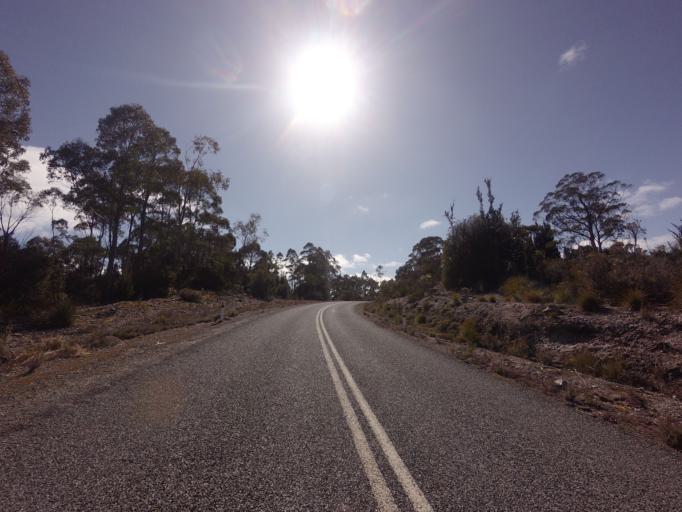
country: AU
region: Tasmania
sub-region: Derwent Valley
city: New Norfolk
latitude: -42.7590
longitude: 146.3985
